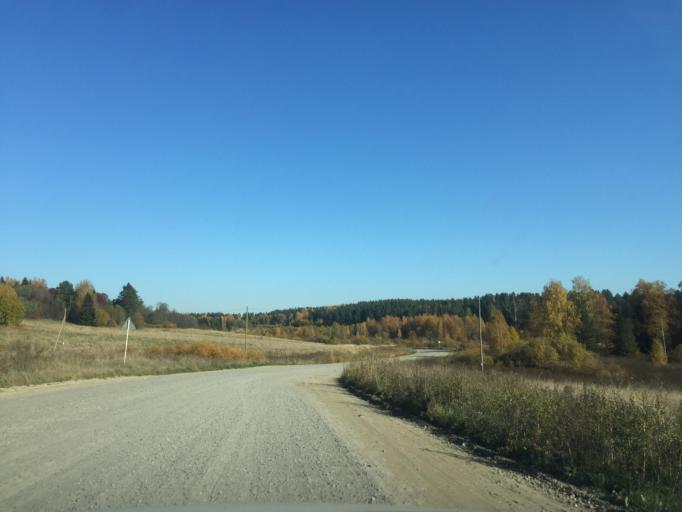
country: RU
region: Leningrad
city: Kuznechnoye
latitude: 61.3086
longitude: 29.9319
